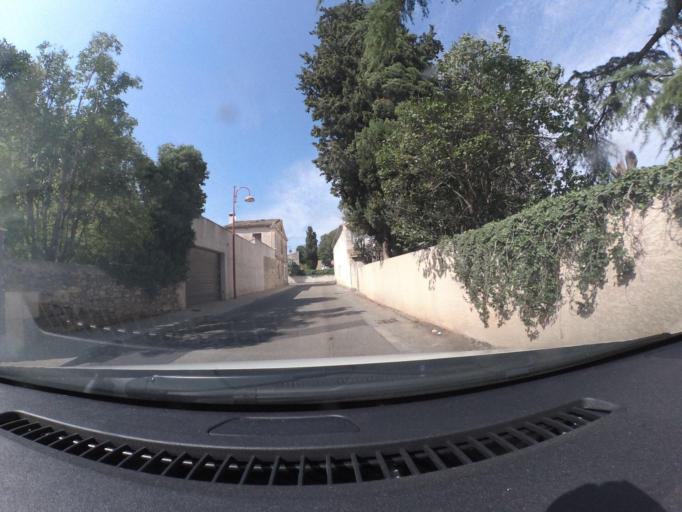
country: FR
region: Languedoc-Roussillon
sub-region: Departement de l'Herault
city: Baillargues
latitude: 43.6576
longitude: 4.0126
